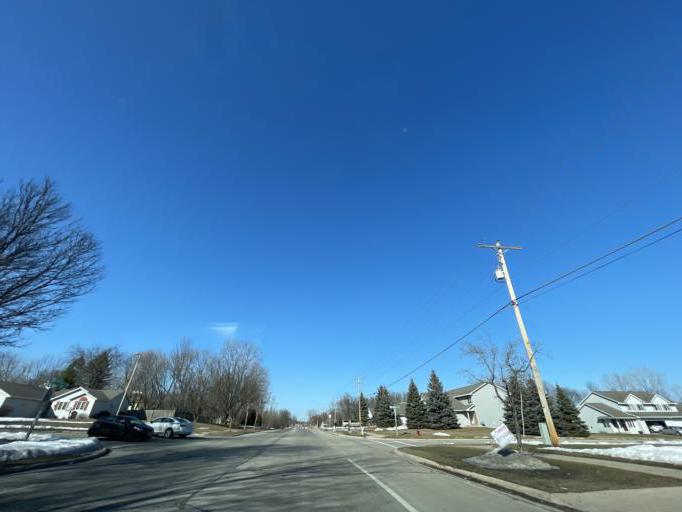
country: US
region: Wisconsin
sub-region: Brown County
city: Howard
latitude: 44.5834
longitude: -88.0844
